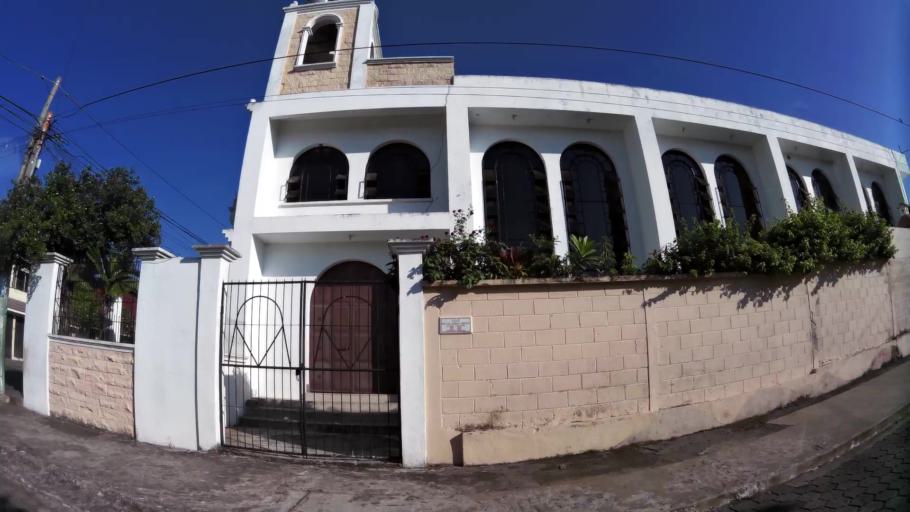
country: GT
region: Suchitepeque
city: Mazatenango
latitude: 14.5297
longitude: -91.5151
